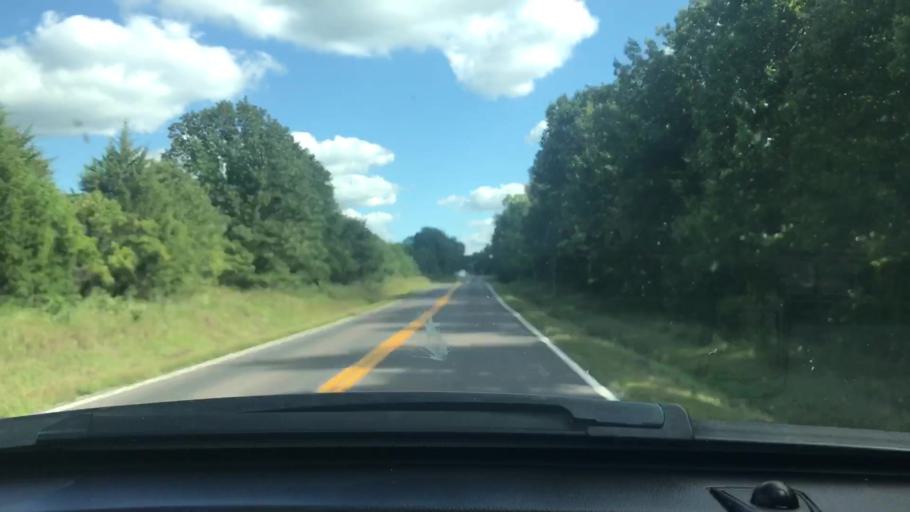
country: US
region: Missouri
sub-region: Wright County
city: Hartville
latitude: 37.3637
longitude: -92.3465
